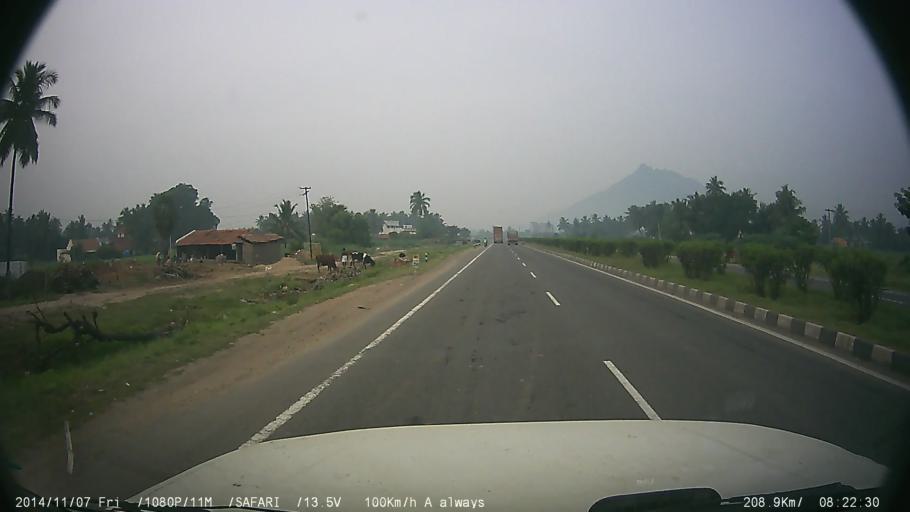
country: IN
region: Tamil Nadu
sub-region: Salem
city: Salem
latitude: 11.6271
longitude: 78.1141
